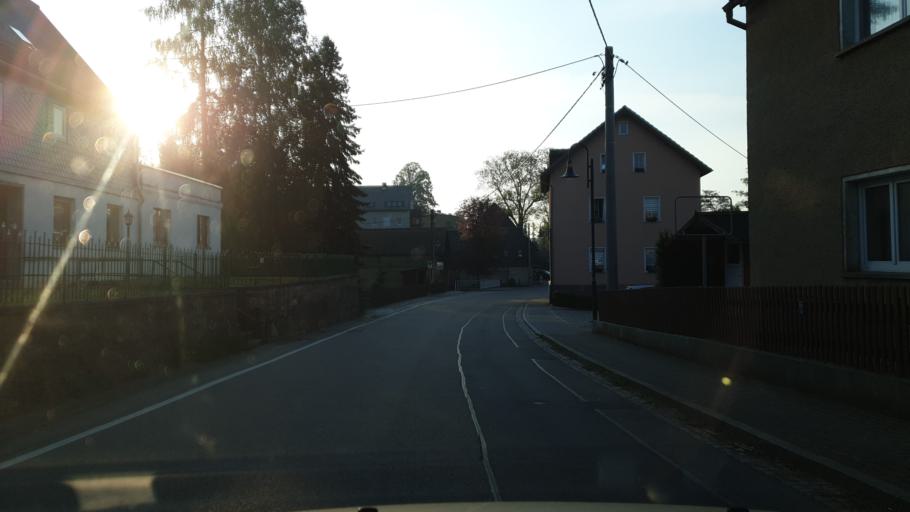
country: DE
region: Saxony
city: Bernsdorf
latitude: 50.7842
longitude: 12.6765
